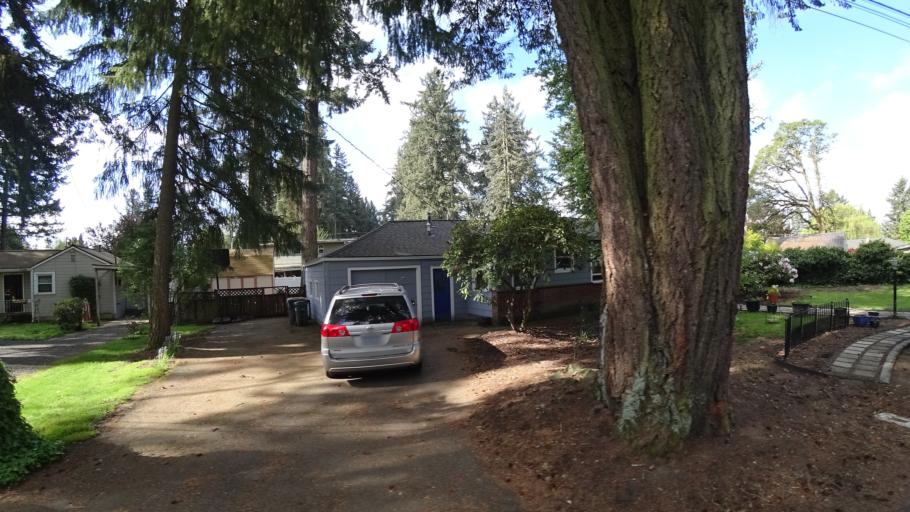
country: US
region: Oregon
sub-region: Washington County
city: Hillsboro
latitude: 45.5131
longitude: -122.9783
